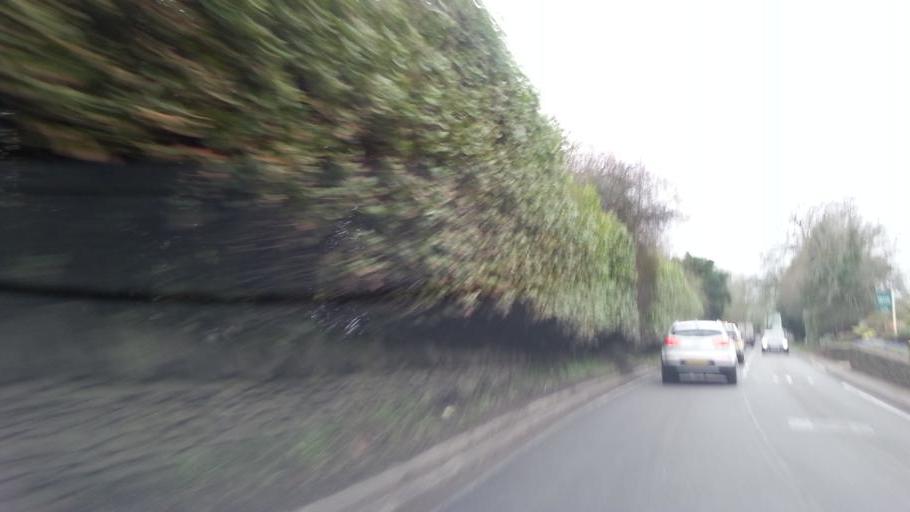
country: GB
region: England
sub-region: Northamptonshire
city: Brackley
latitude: 52.0533
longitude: -1.2215
